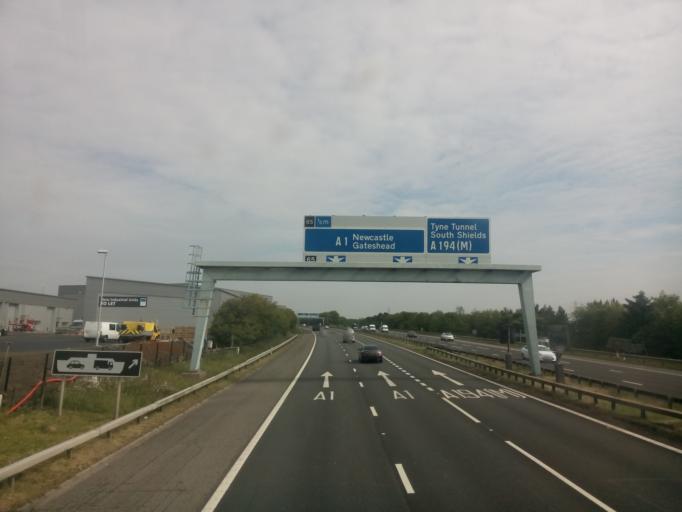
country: GB
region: England
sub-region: County Durham
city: Chester-le-Street
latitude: 54.8947
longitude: -1.5592
